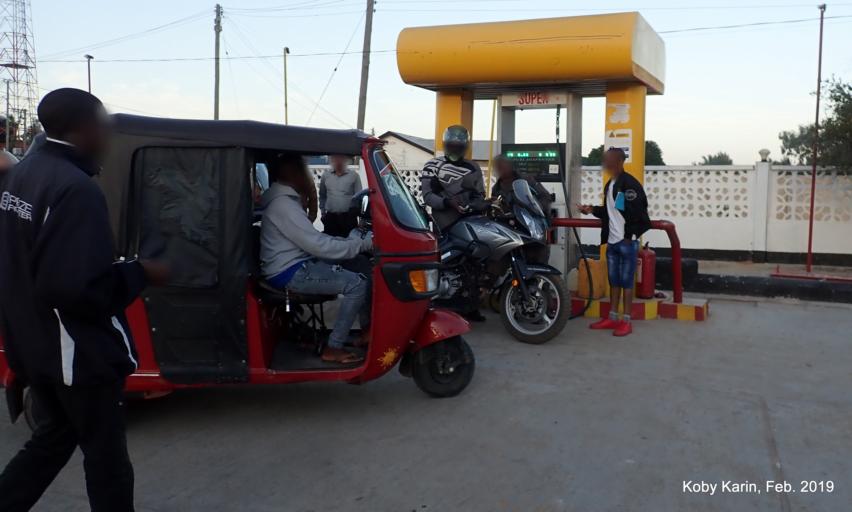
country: TZ
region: Singida
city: Singida
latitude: -4.8206
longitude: 34.7641
